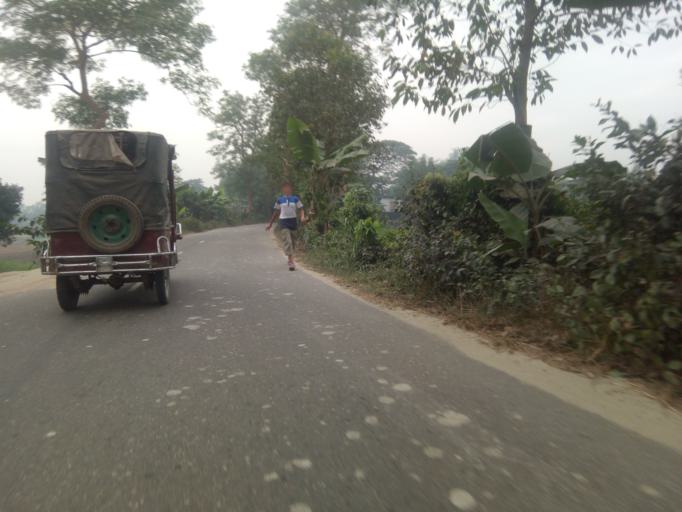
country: BD
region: Dhaka
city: Narayanganj
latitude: 23.5320
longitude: 90.4838
